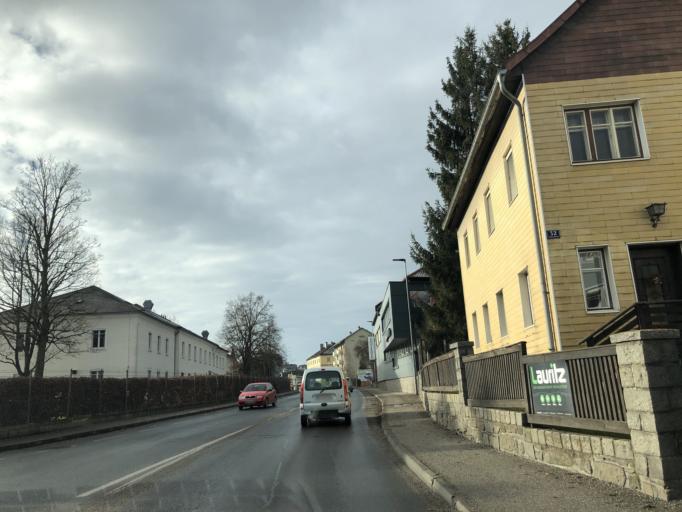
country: AT
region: Upper Austria
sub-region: Politischer Bezirk Freistadt
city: Freistadt
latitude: 48.5045
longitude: 14.5030
